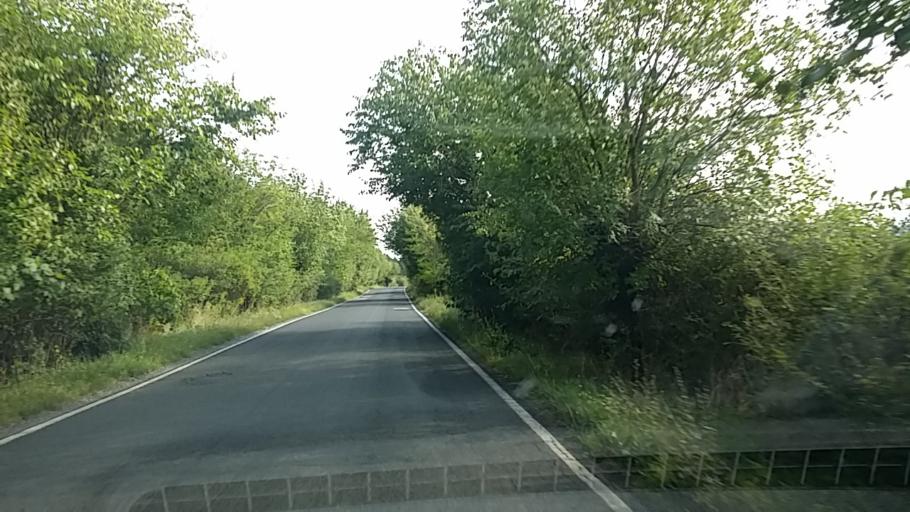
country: HU
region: Gyor-Moson-Sopron
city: Fertorakos
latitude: 47.7404
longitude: 16.6210
